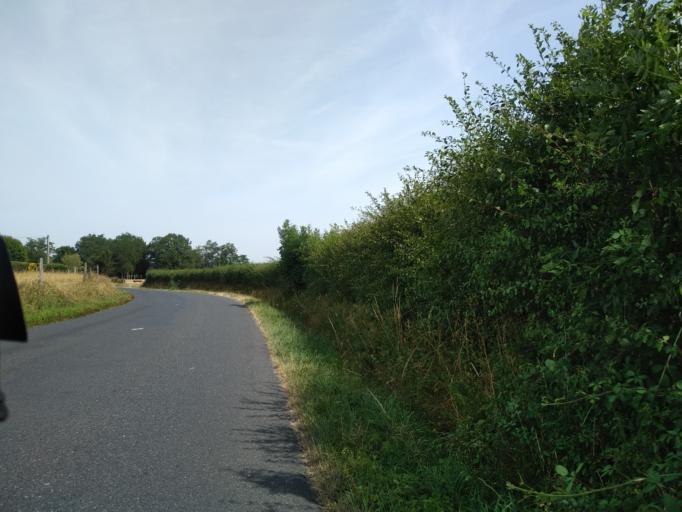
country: FR
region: Bourgogne
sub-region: Departement de Saone-et-Loire
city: Digoin
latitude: 46.4416
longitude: 3.9747
